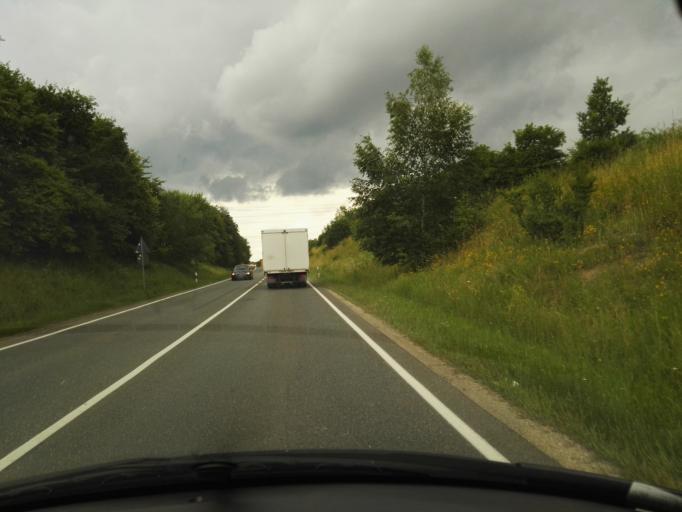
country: DE
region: Bavaria
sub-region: Upper Franconia
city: Redwitz an der Rodach
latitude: 50.1595
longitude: 11.1934
